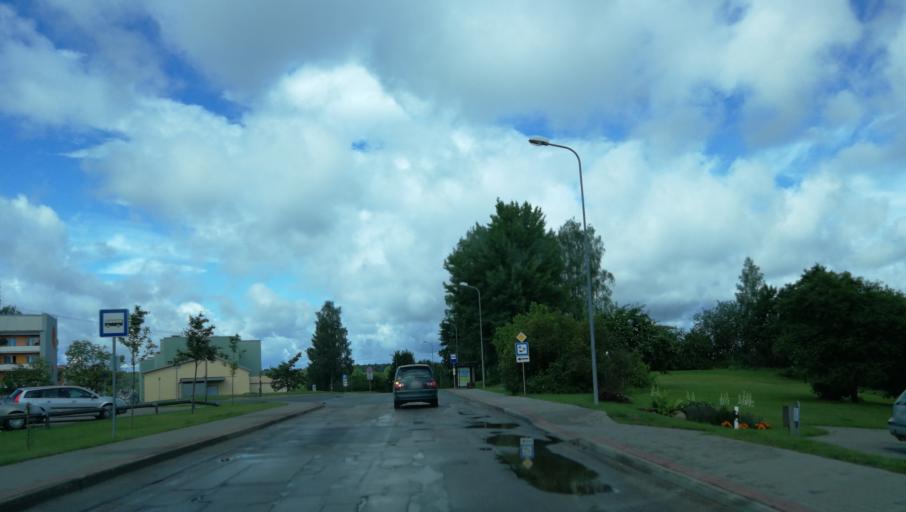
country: LV
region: Cesu Rajons
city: Cesis
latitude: 57.3150
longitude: 25.2589
